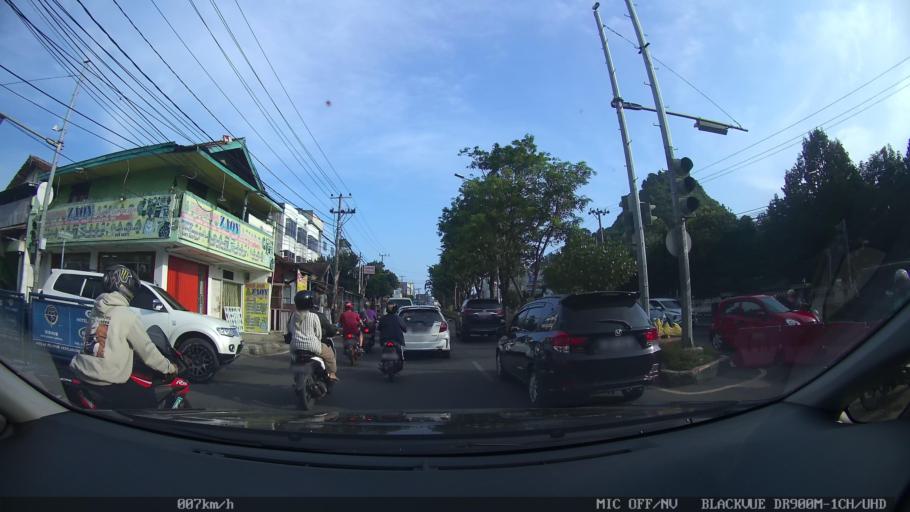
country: ID
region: Lampung
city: Kedaton
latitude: -5.3875
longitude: 105.2617
